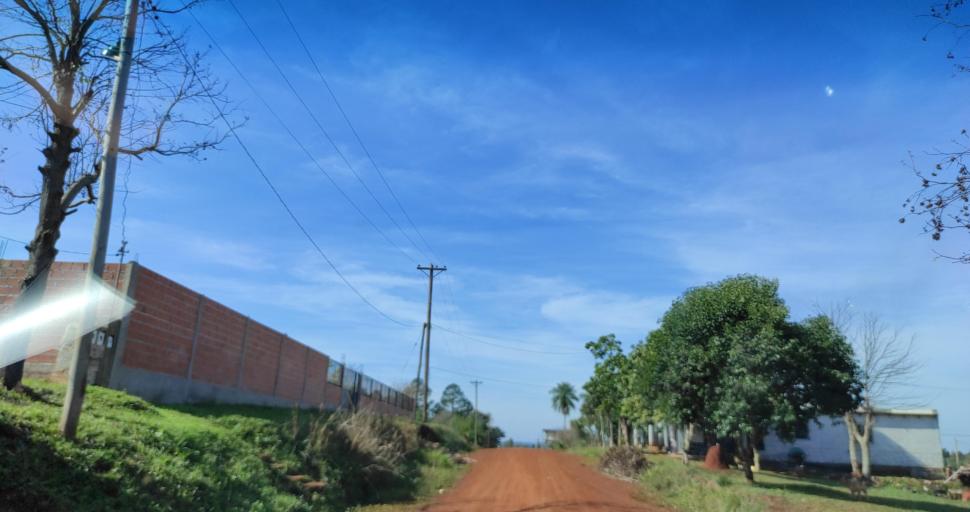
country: AR
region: Misiones
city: Garupa
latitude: -27.4866
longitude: -55.8296
